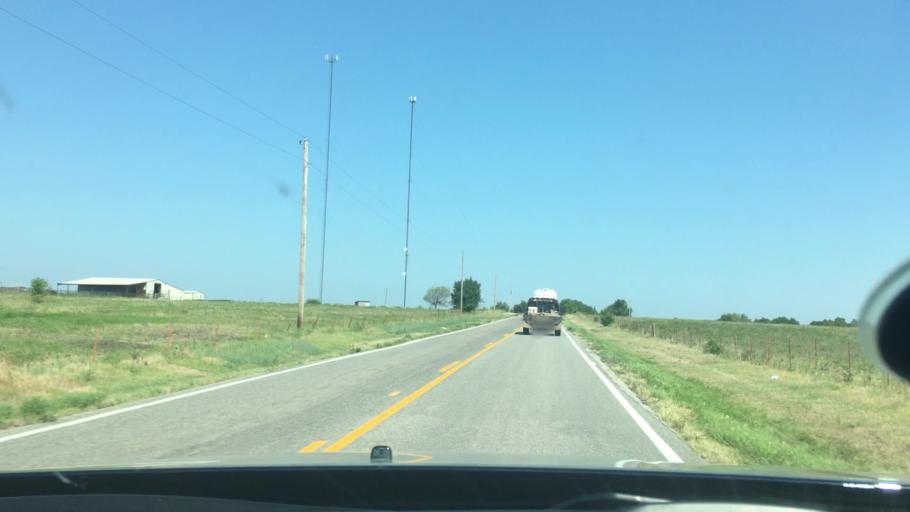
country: US
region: Oklahoma
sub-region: Johnston County
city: Tishomingo
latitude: 34.1918
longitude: -96.5330
